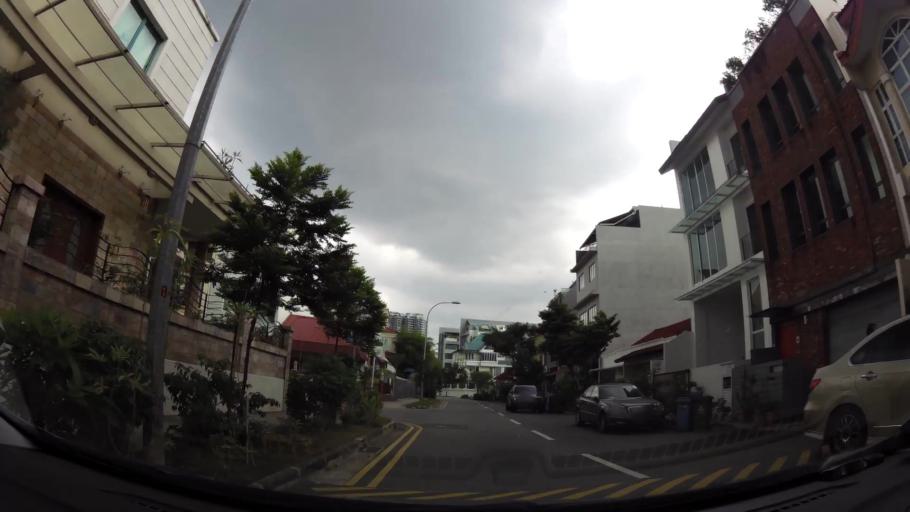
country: SG
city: Singapore
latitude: 1.3139
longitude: 103.8475
